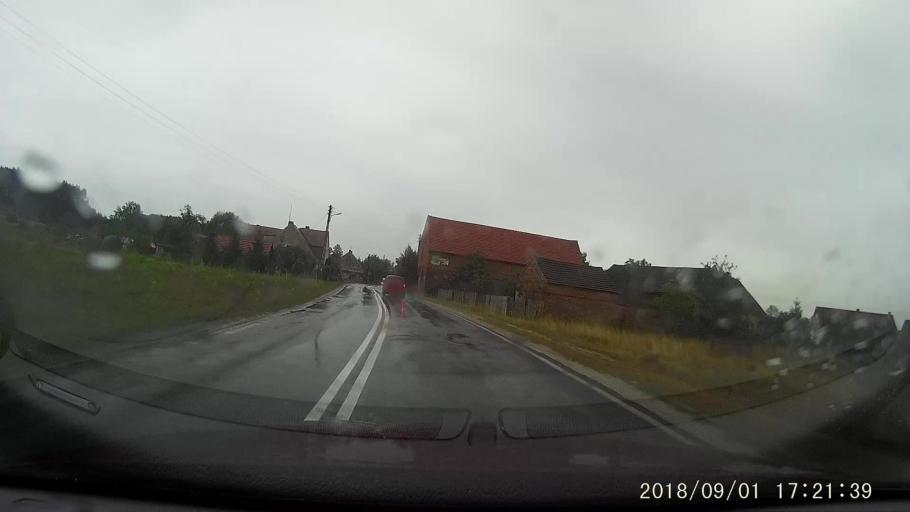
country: PL
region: Lubusz
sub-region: Powiat zaganski
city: Zagan
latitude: 51.7112
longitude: 15.2855
